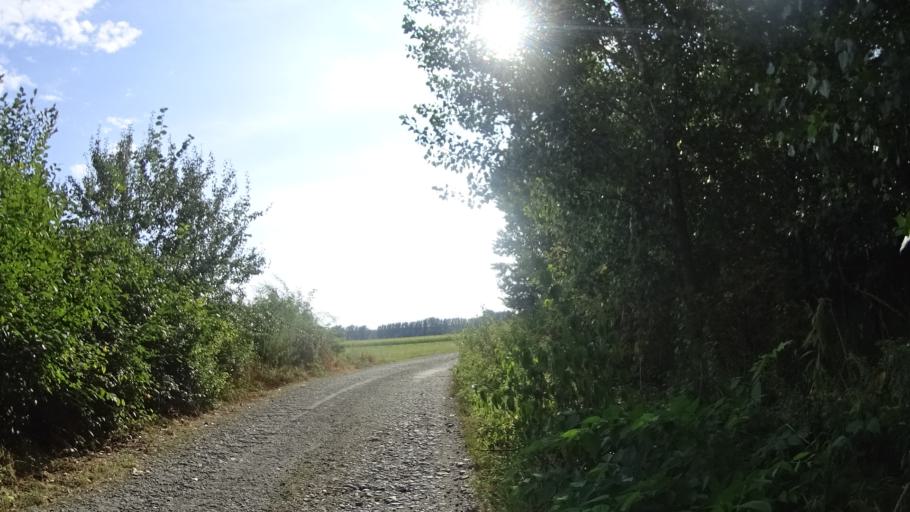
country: SK
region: Trnavsky
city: Gabcikovo
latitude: 47.9276
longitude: 17.4873
